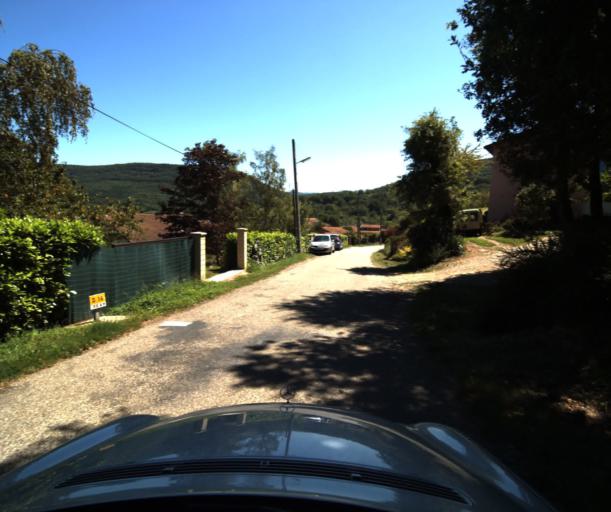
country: FR
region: Midi-Pyrenees
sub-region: Departement de l'Ariege
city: Lavelanet
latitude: 42.9593
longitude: 1.9009
